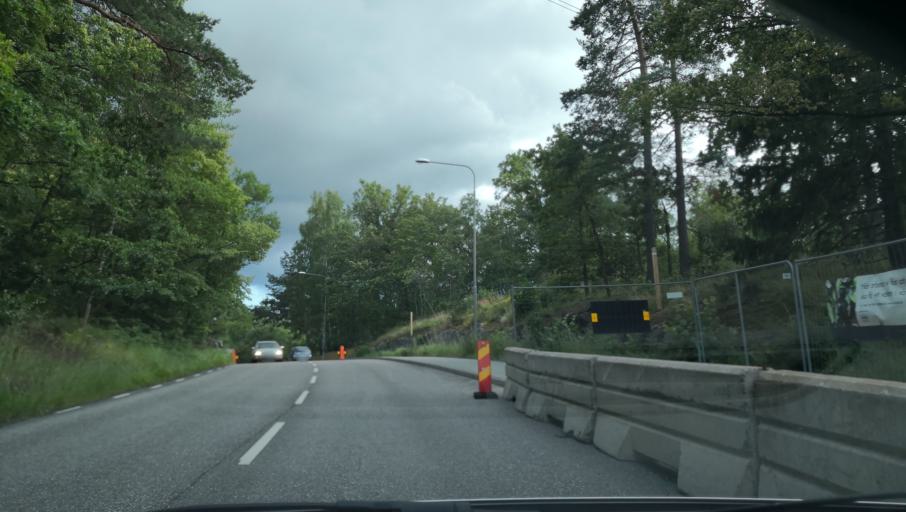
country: SE
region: Stockholm
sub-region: Stockholms Kommun
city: Arsta
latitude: 59.2527
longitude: 18.0492
